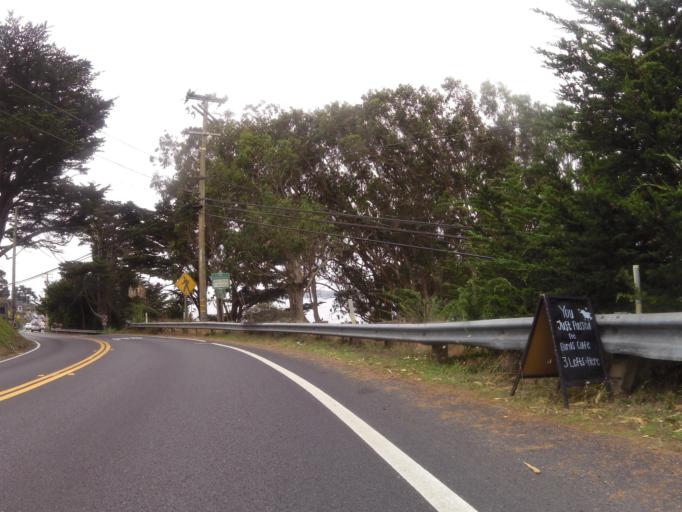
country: US
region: California
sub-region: Sonoma County
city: Bodega Bay
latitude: 38.3354
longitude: -123.0494
